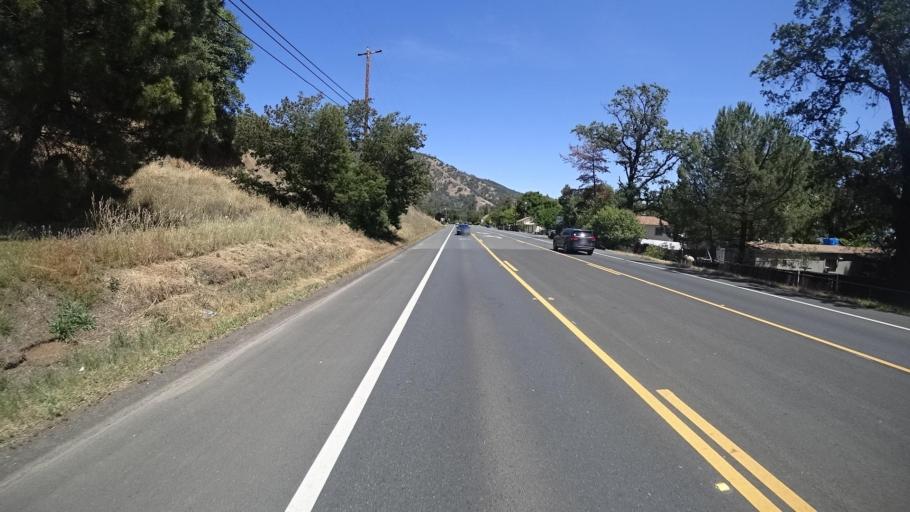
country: US
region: California
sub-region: Lake County
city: Nice
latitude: 39.1230
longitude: -122.8505
